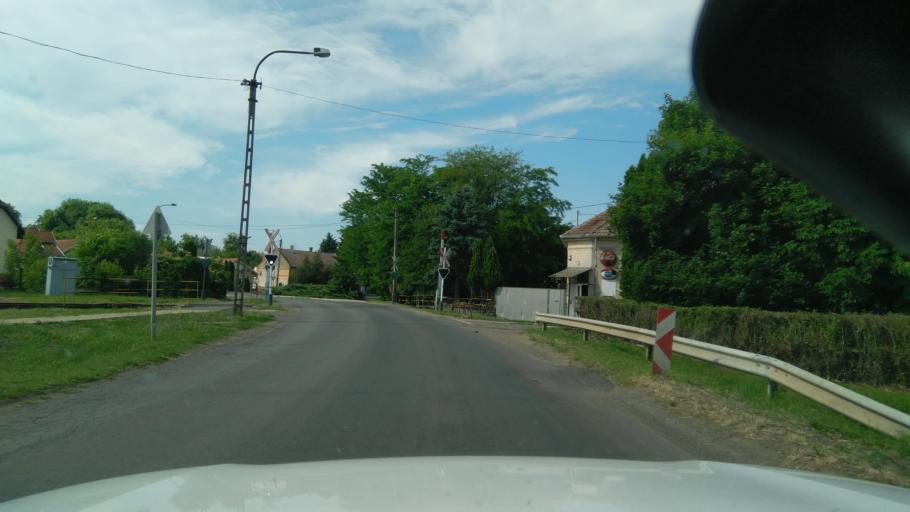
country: HU
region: Bekes
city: Medgyesegyhaza
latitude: 46.4973
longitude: 21.0324
